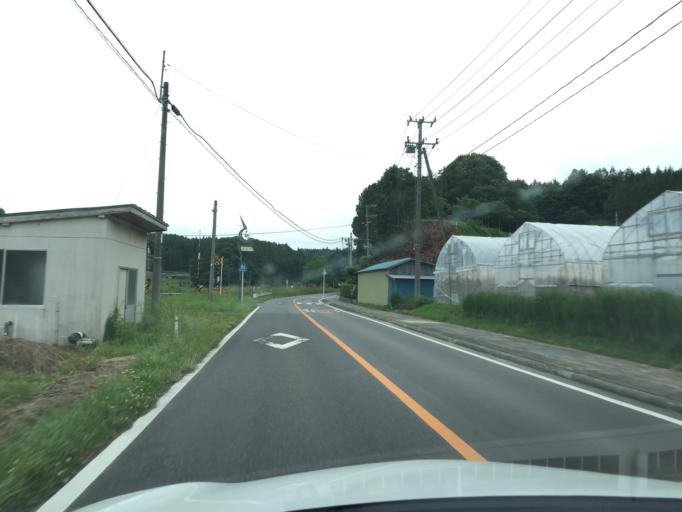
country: JP
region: Fukushima
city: Funehikimachi-funehiki
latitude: 37.3112
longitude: 140.6580
